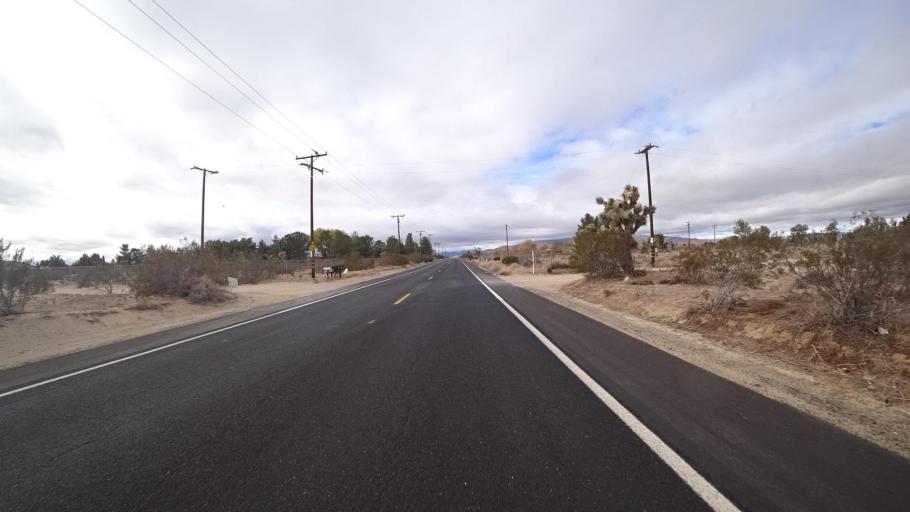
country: US
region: California
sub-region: Kern County
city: Rosamond
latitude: 34.9509
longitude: -118.2339
